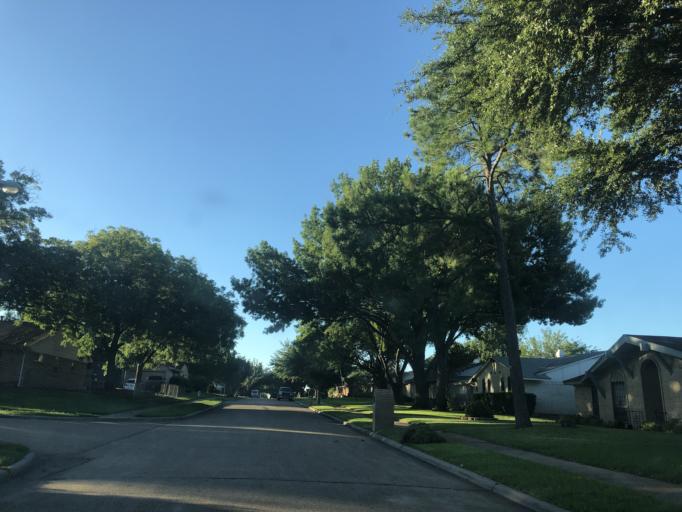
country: US
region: Texas
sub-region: Dallas County
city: Garland
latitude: 32.8371
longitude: -96.6409
